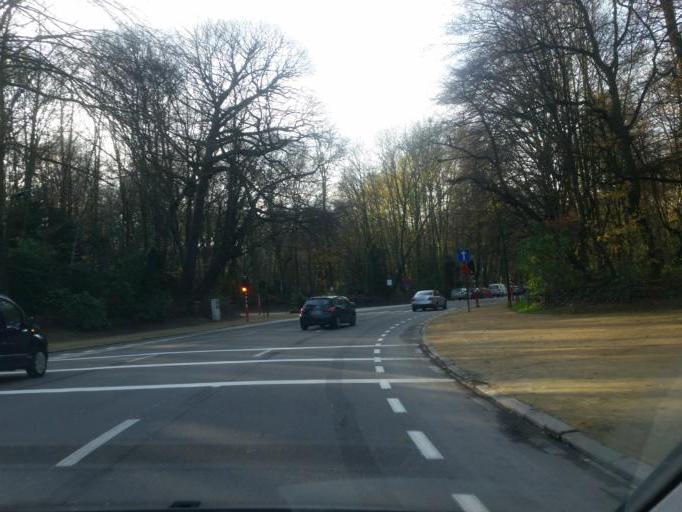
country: BE
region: Brussels Capital
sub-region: Bruxelles-Capitale
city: Brussels
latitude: 50.8141
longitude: 4.3724
